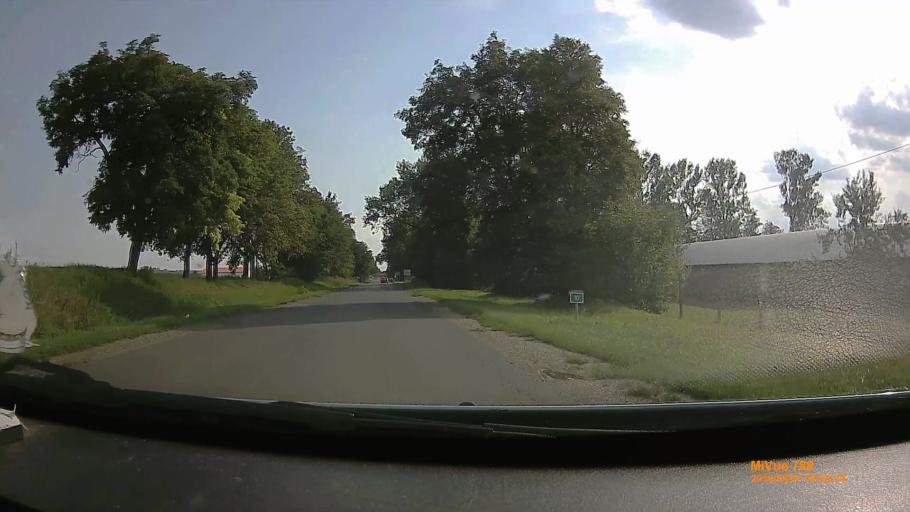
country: HU
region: Borsod-Abauj-Zemplen
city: Gonc
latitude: 48.3948
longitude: 21.2232
